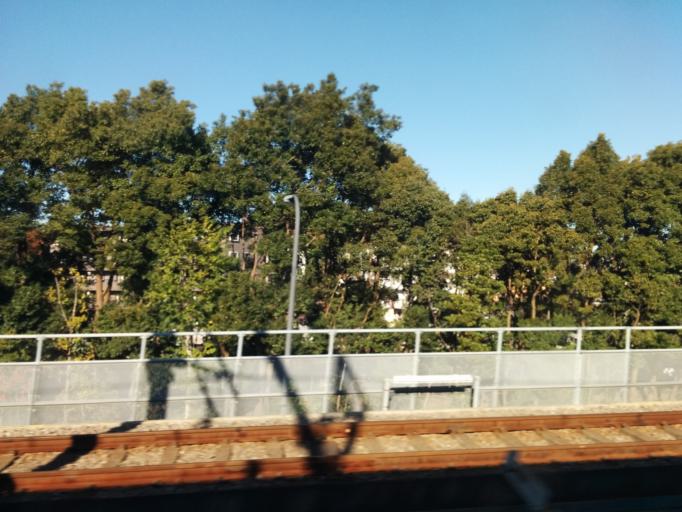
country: JP
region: Kanagawa
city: Yokohama
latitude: 35.4979
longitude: 139.6059
